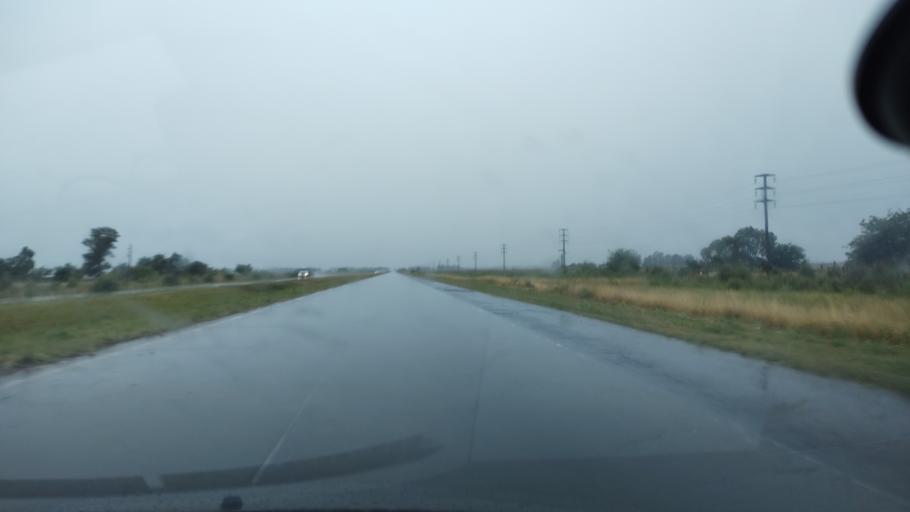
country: AR
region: Buenos Aires
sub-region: Partido de San Vicente
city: San Vicente
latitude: -35.0647
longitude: -58.4787
